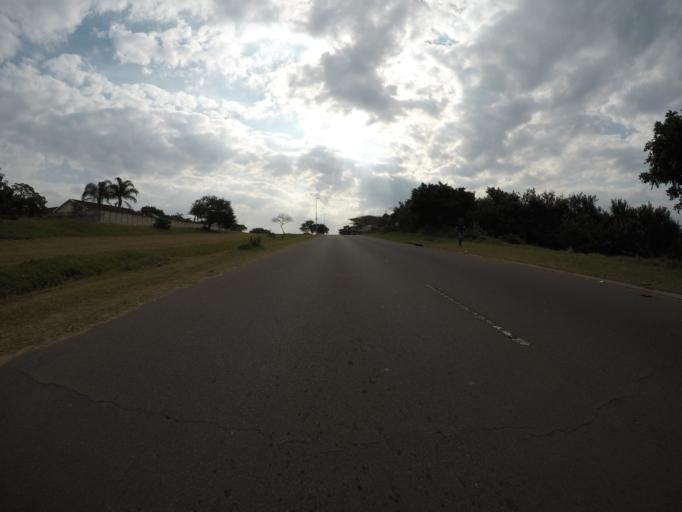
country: ZA
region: KwaZulu-Natal
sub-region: uThungulu District Municipality
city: Richards Bay
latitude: -28.7437
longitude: 32.0830
